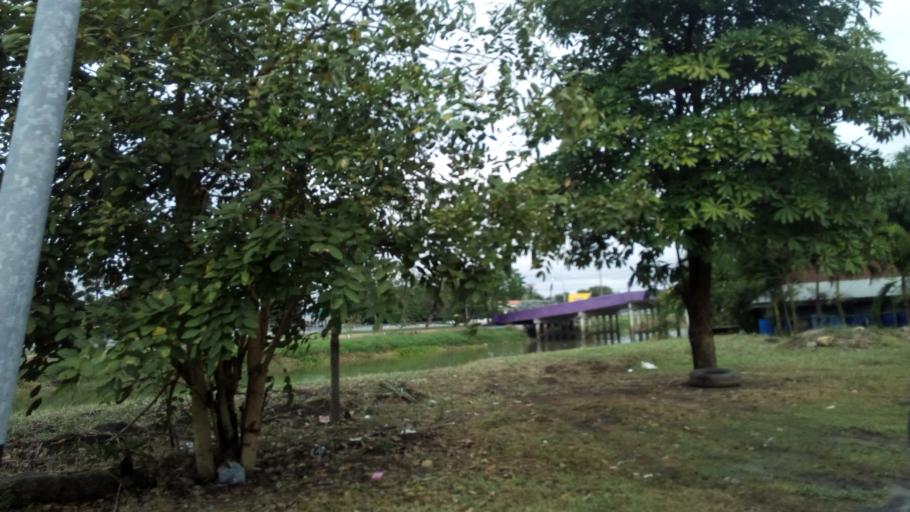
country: TH
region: Pathum Thani
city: Nong Suea
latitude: 14.0707
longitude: 100.8777
